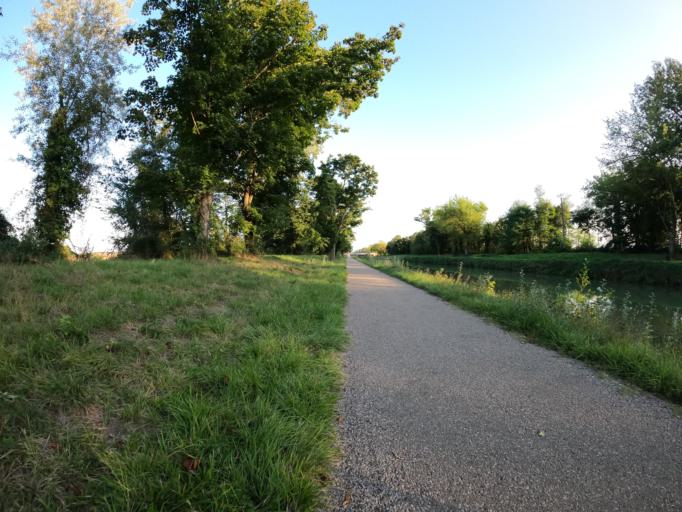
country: FR
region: Midi-Pyrenees
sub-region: Departement du Tarn-et-Garonne
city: Saint-Porquier
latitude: 44.0076
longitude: 1.1822
